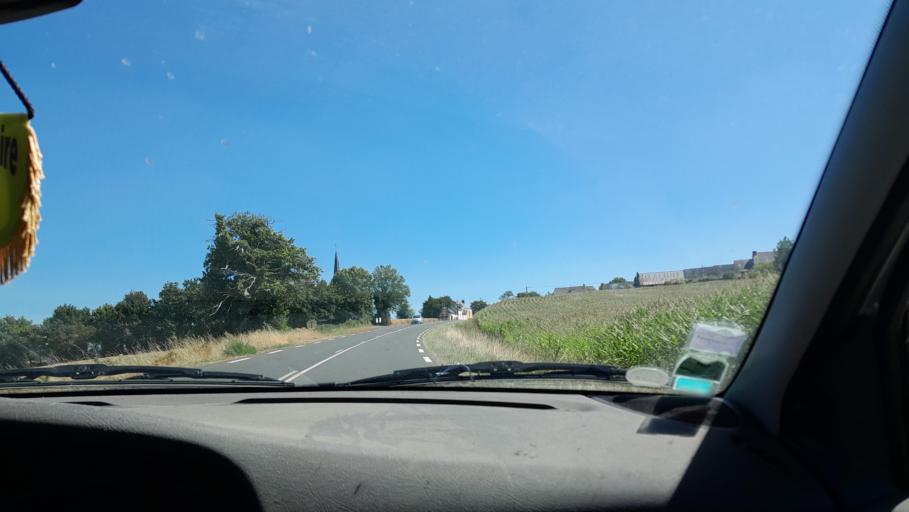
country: FR
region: Pays de la Loire
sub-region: Departement de la Loire-Atlantique
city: Saint-Mars-la-Jaille
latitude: 47.5846
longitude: -1.1930
